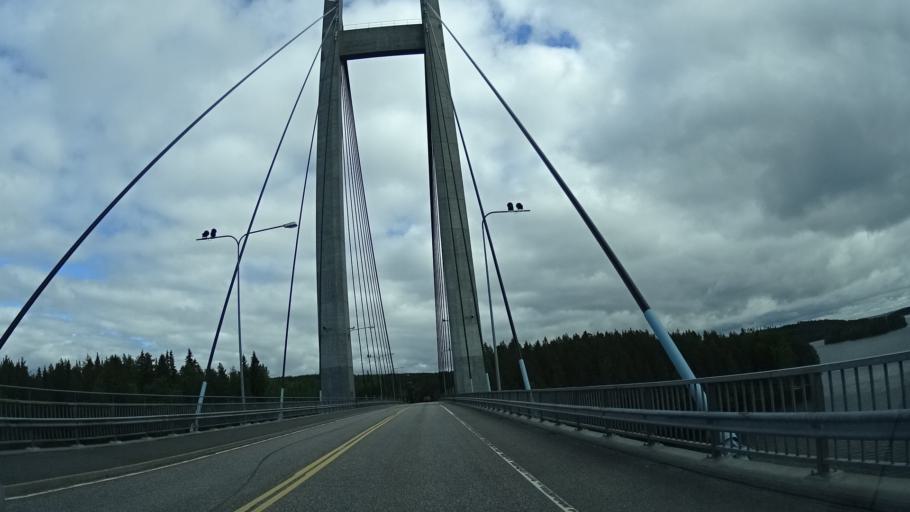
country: FI
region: Central Finland
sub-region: Jyvaeskylae
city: Korpilahti
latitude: 61.9987
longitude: 25.6765
